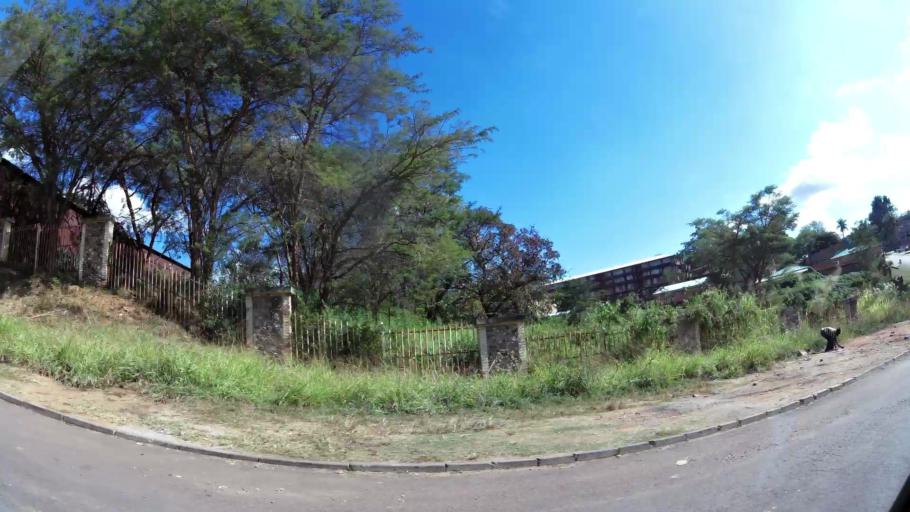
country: ZA
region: Limpopo
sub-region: Mopani District Municipality
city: Tzaneen
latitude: -23.8317
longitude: 30.1605
